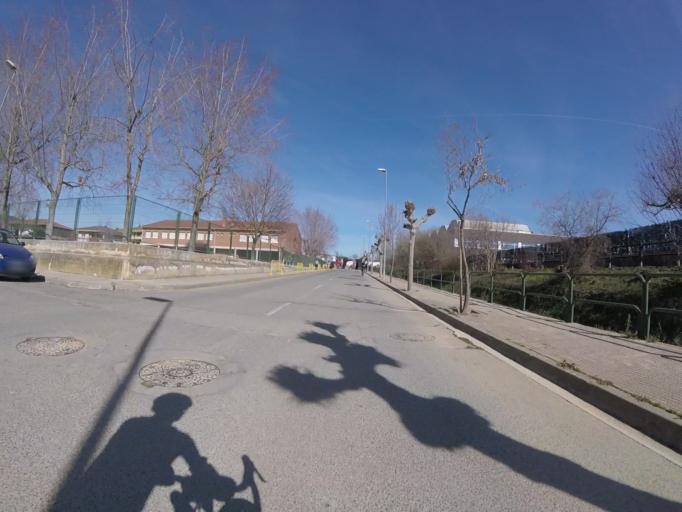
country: ES
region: Navarre
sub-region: Provincia de Navarra
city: Villatuerta
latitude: 42.6604
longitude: -1.9902
